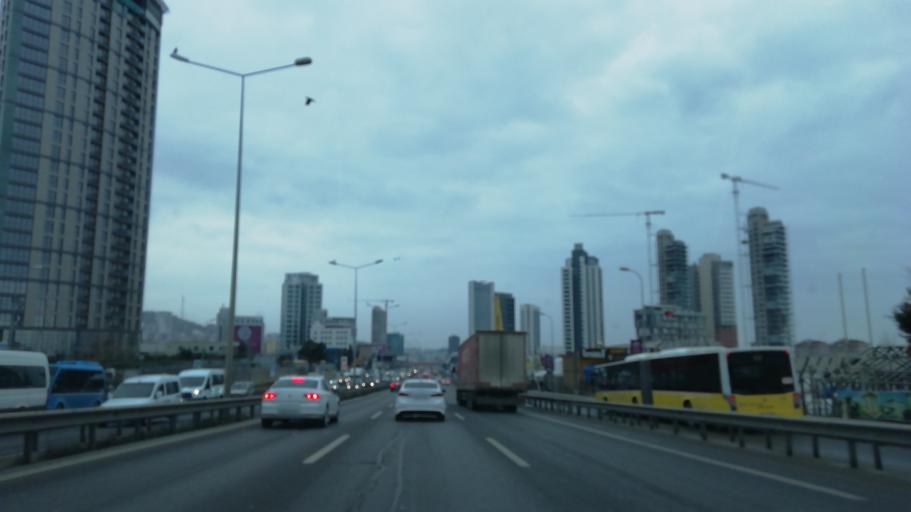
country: TR
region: Istanbul
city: Pendik
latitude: 40.9037
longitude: 29.2149
